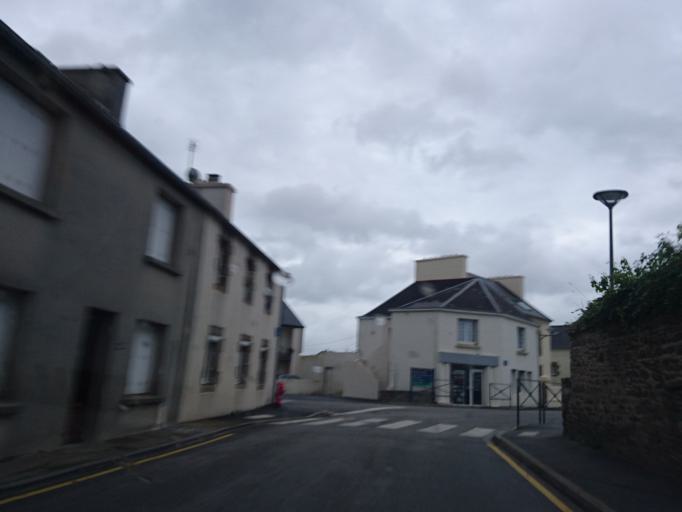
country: FR
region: Brittany
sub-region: Departement du Finistere
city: Le Conquet
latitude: 48.3583
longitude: -4.7723
